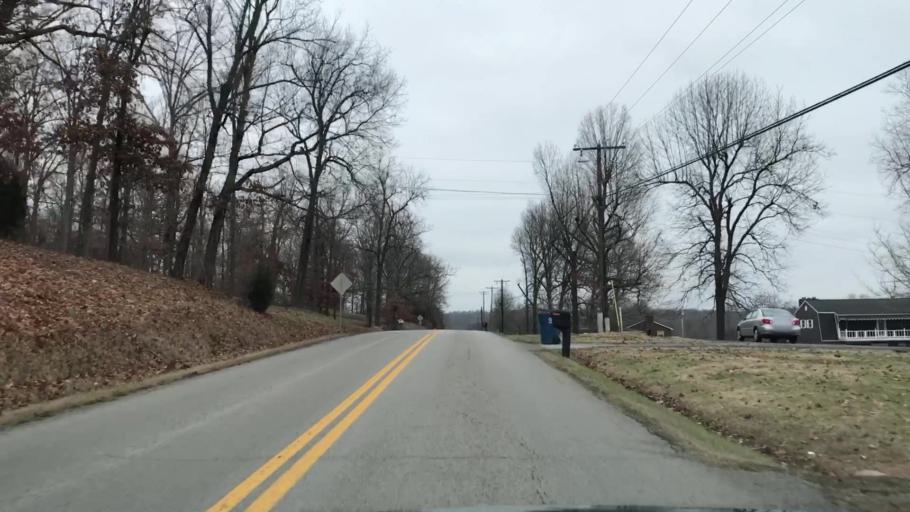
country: US
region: Kentucky
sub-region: Muhlenberg County
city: Greenville
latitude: 37.2262
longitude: -87.1935
